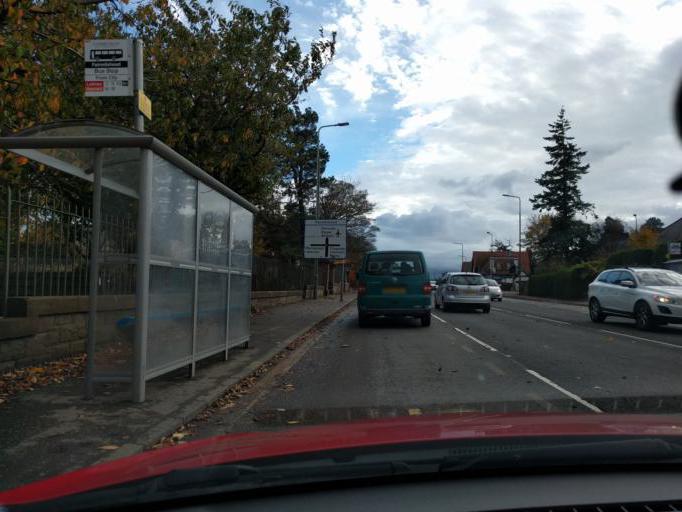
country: GB
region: Scotland
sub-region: Edinburgh
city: Edinburgh
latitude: 55.9023
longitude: -3.2050
